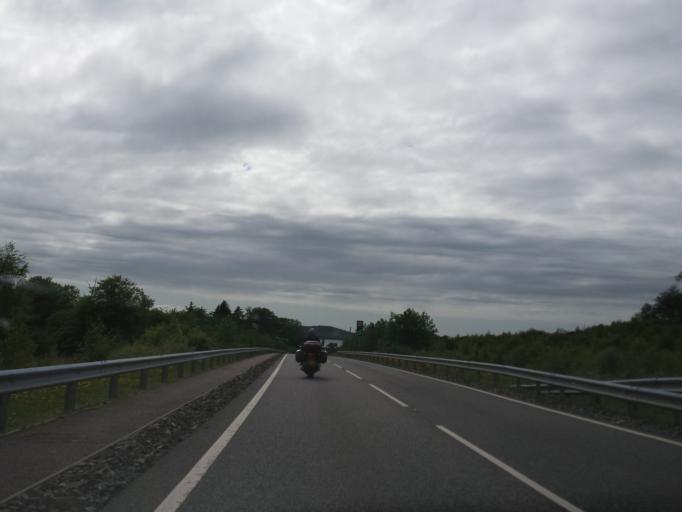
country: GB
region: Scotland
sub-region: Argyll and Bute
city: Isle Of Mull
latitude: 56.9124
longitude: -5.8266
